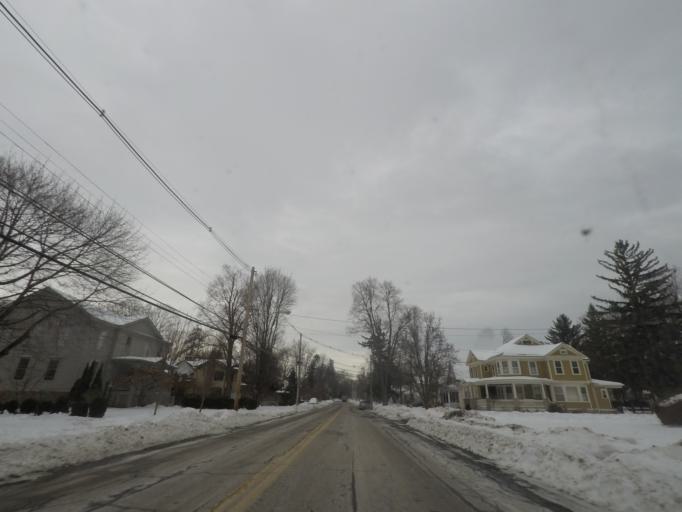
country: US
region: New York
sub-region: Columbia County
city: Kinderhook
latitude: 42.3973
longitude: -73.6998
